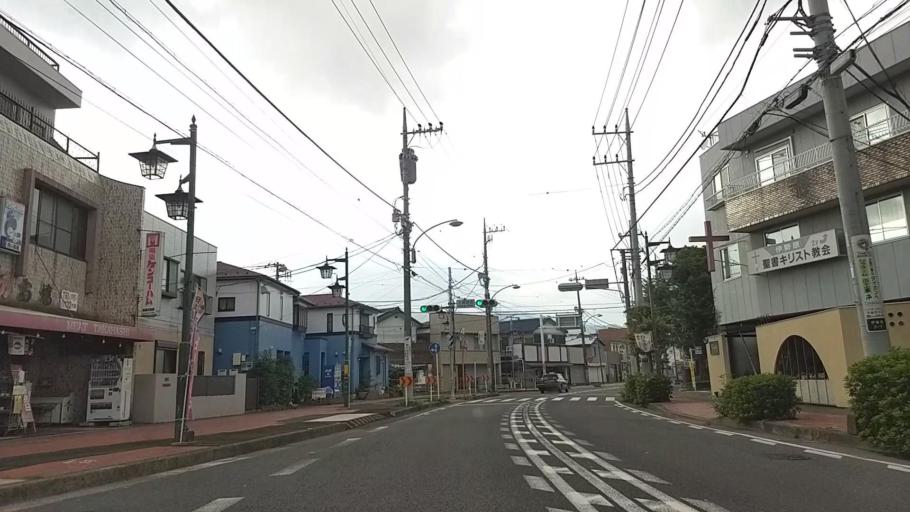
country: JP
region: Kanagawa
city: Isehara
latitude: 35.3989
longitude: 139.3054
